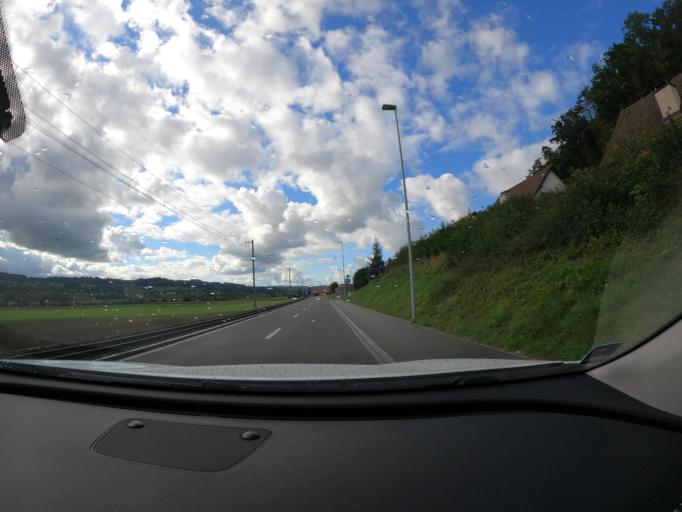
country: CH
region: Aargau
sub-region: Bezirk Kulm
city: Gontenschwil
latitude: 47.2737
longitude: 8.1637
